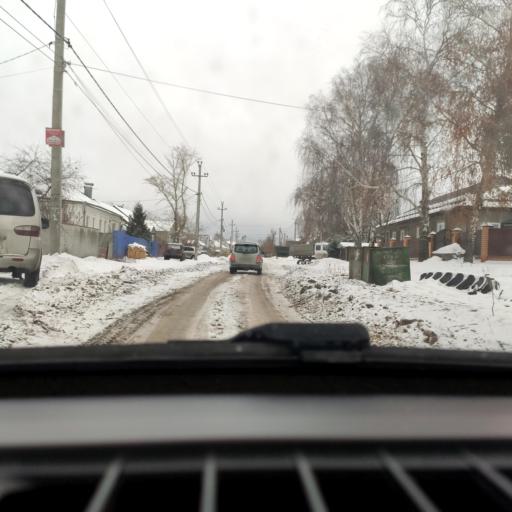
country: RU
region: Voronezj
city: Podgornoye
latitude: 51.7349
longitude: 39.1440
